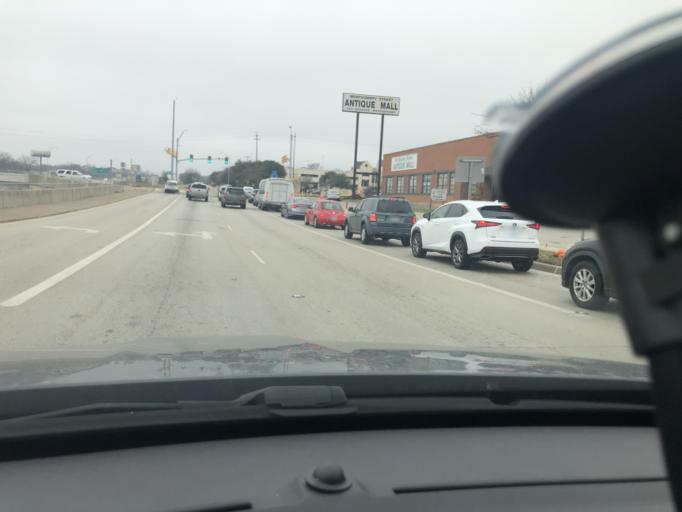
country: US
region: Texas
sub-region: Tarrant County
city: Westworth
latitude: 32.7333
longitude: -97.3689
